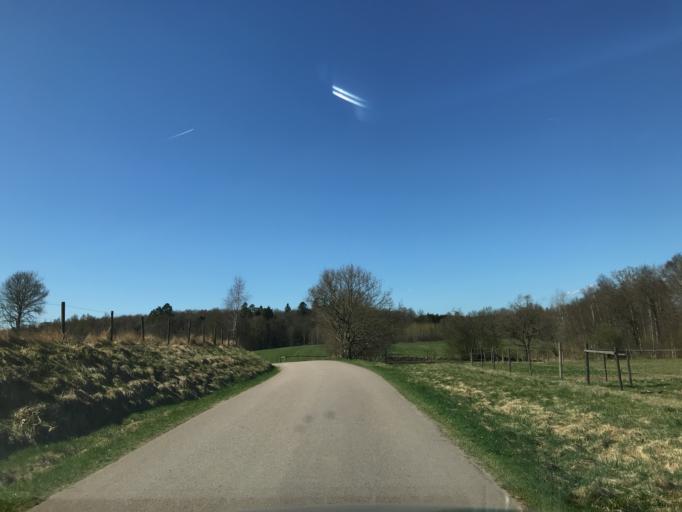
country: SE
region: Skane
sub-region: Klippans Kommun
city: Ljungbyhed
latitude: 56.0688
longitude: 13.2835
